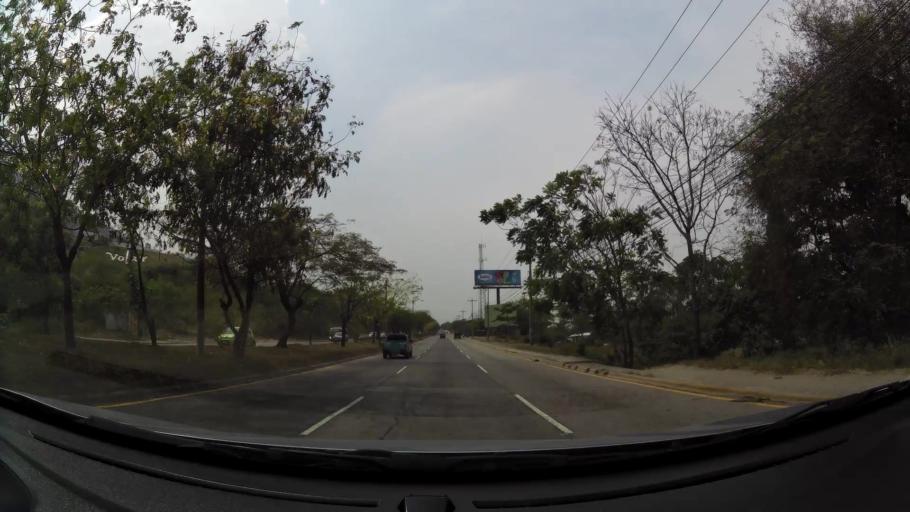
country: HN
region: Cortes
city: Chotepe
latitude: 15.4481
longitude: -88.0221
